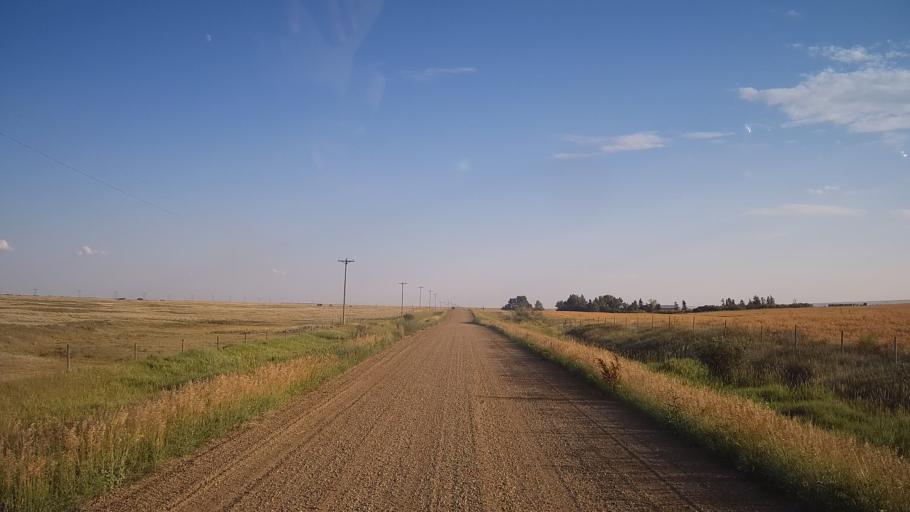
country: CA
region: Alberta
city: Hanna
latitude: 51.6171
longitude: -111.8568
